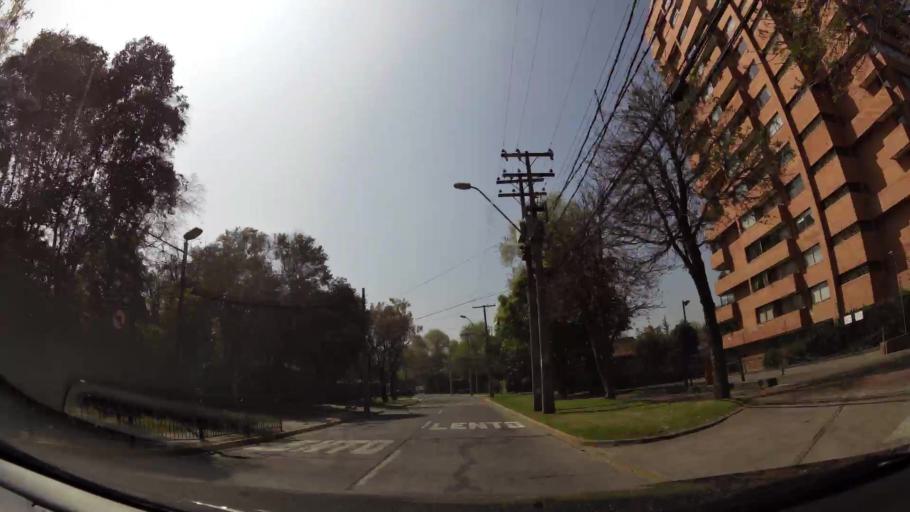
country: CL
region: Santiago Metropolitan
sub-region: Provincia de Santiago
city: Villa Presidente Frei, Nunoa, Santiago, Chile
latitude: -33.3963
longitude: -70.5869
